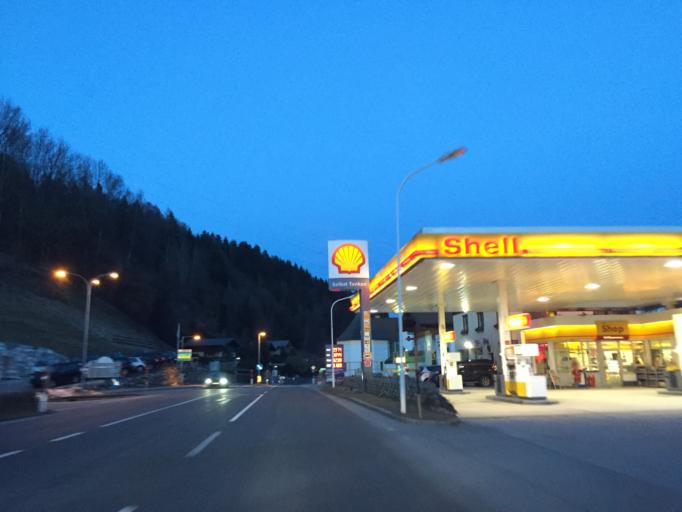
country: AT
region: Salzburg
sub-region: Politischer Bezirk Zell am See
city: Taxenbach
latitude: 47.2931
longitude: 12.9686
